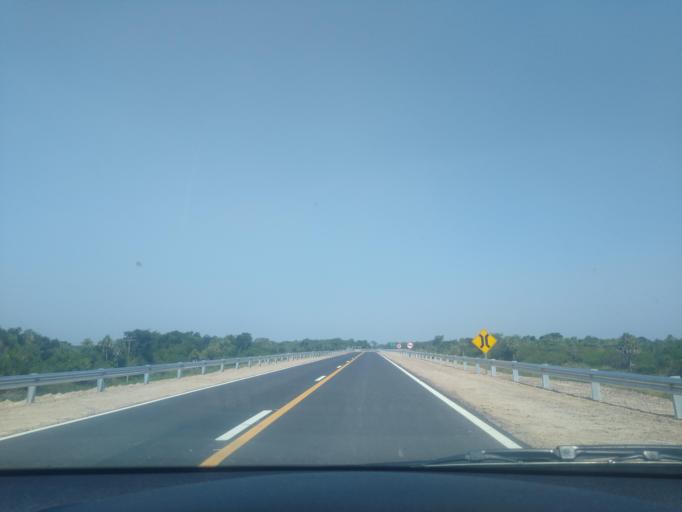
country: AR
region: Chaco
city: Puerto Tirol
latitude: -27.5716
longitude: -59.2630
